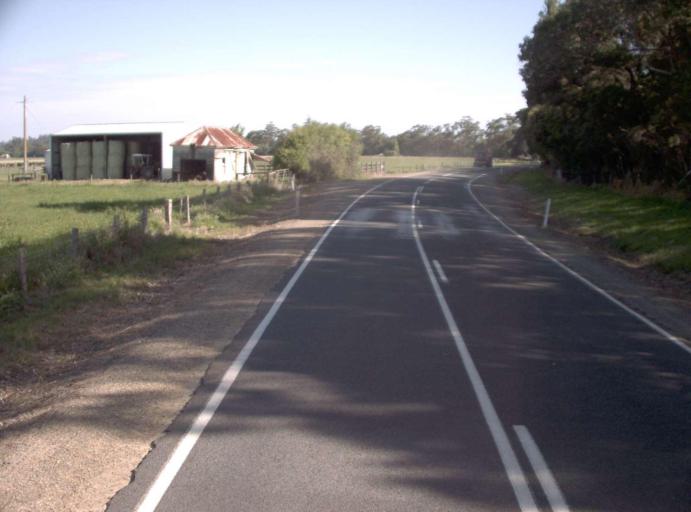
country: AU
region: Victoria
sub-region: East Gippsland
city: Lakes Entrance
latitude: -37.7329
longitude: 148.5049
